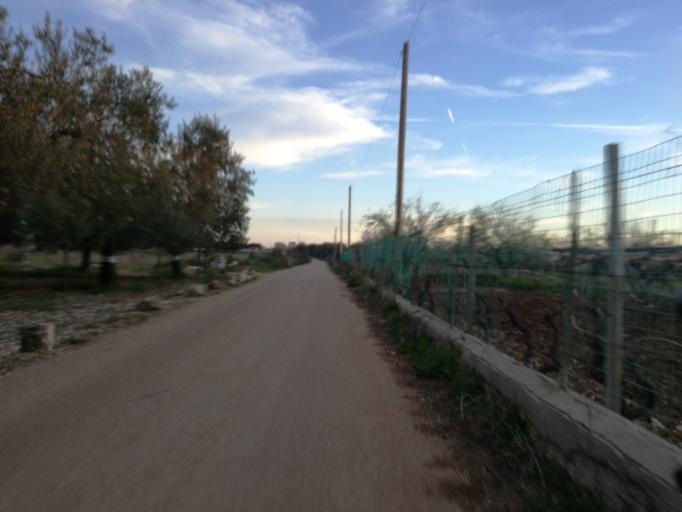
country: IT
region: Apulia
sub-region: Provincia di Bari
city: Adelfia
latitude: 41.0143
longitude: 16.8716
